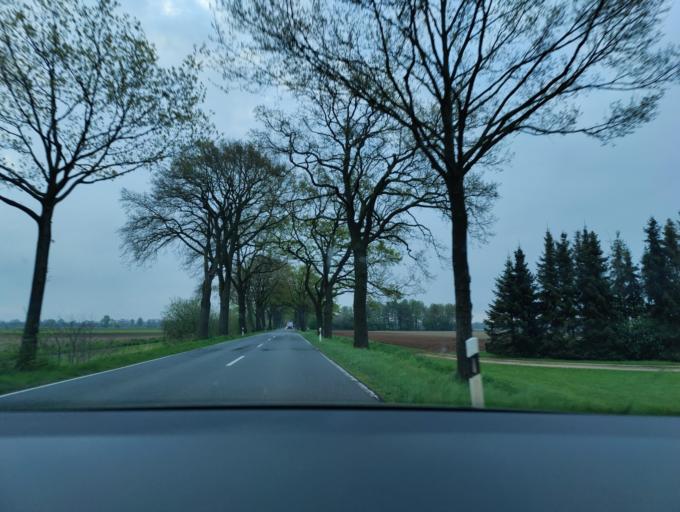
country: DE
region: Lower Saxony
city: Wietmarschen
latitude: 52.5092
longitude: 7.1595
